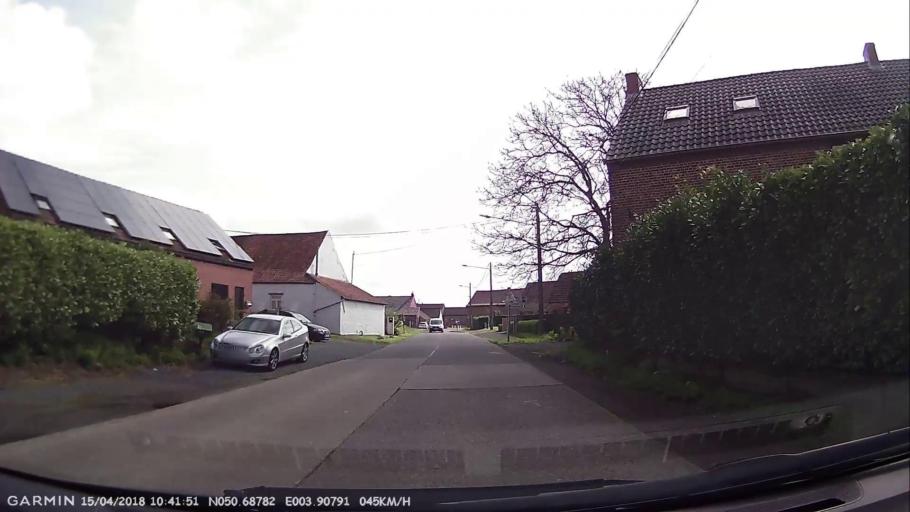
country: BE
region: Wallonia
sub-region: Province du Hainaut
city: Silly
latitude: 50.6878
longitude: 3.9080
